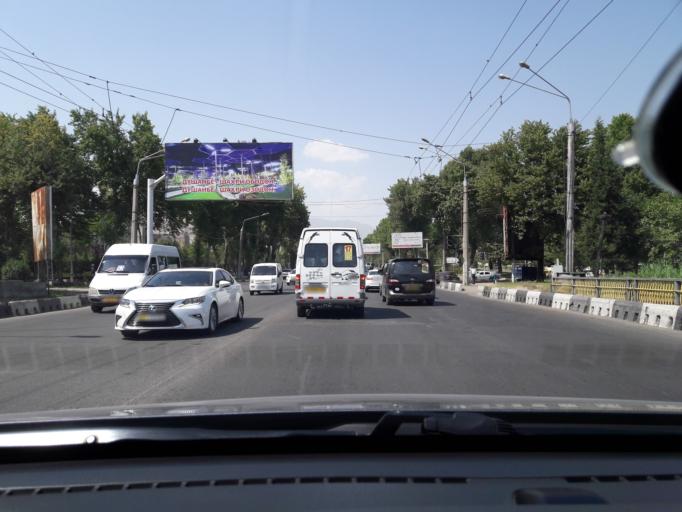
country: TJ
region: Dushanbe
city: Dushanbe
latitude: 38.5770
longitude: 68.7549
